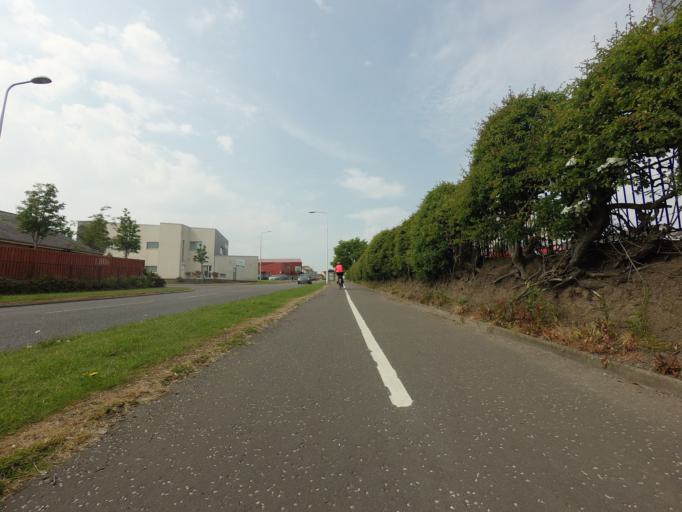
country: GB
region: Scotland
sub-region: Fife
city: Townhill
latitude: 56.0653
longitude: -3.4149
